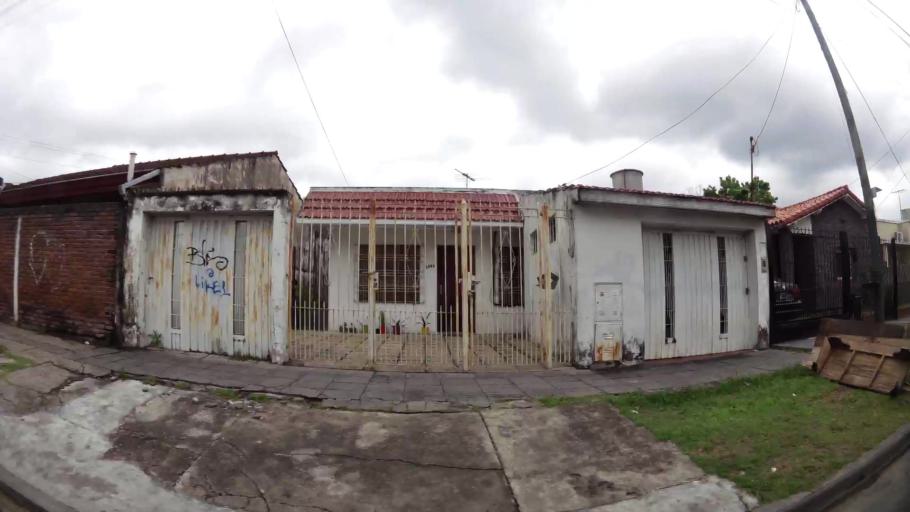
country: AR
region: Buenos Aires
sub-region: Partido de Lomas de Zamora
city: Lomas de Zamora
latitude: -34.7556
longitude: -58.3756
